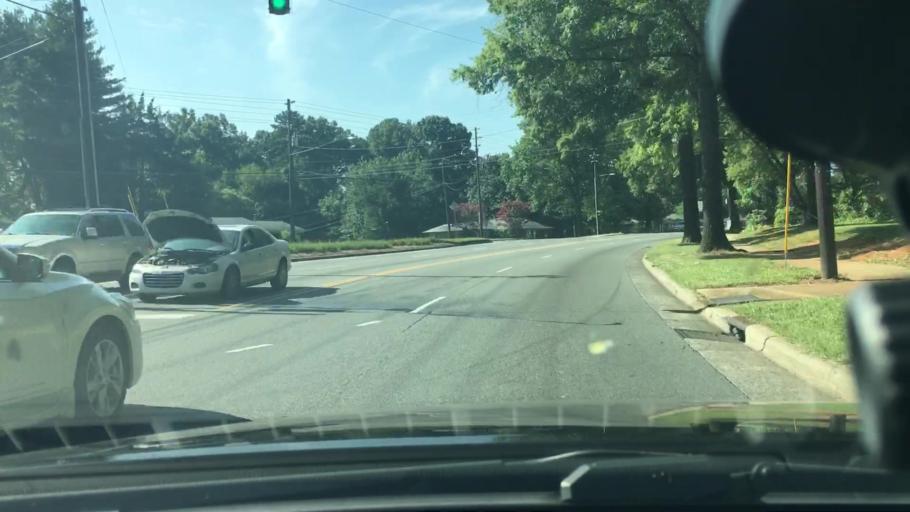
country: US
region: North Carolina
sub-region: Mecklenburg County
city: Matthews
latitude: 35.1942
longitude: -80.7257
